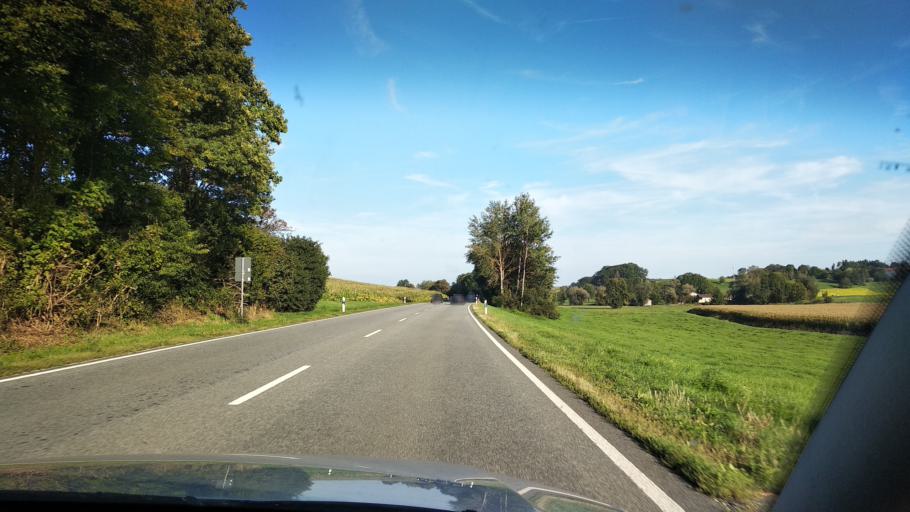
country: DE
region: Bavaria
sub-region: Upper Bavaria
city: Steinhoring
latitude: 48.0851
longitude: 12.0138
